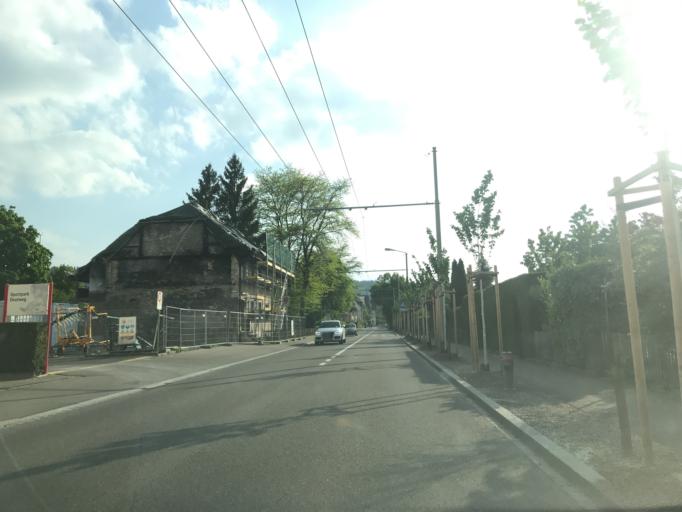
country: CH
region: Zurich
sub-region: Bezirk Winterthur
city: Mattenbach (Kreis 7) / Deutweg
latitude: 47.4957
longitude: 8.7449
